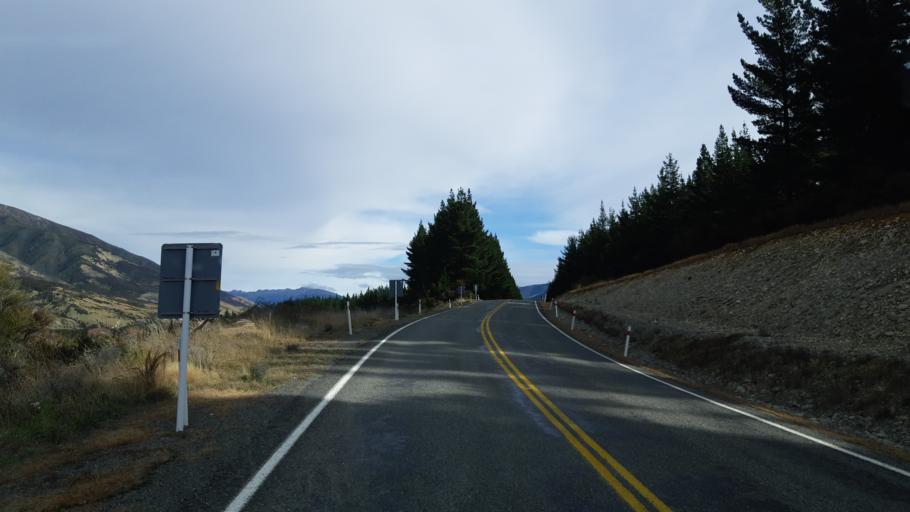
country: NZ
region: Tasman
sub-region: Tasman District
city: Wakefield
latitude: -41.7161
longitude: 173.0801
